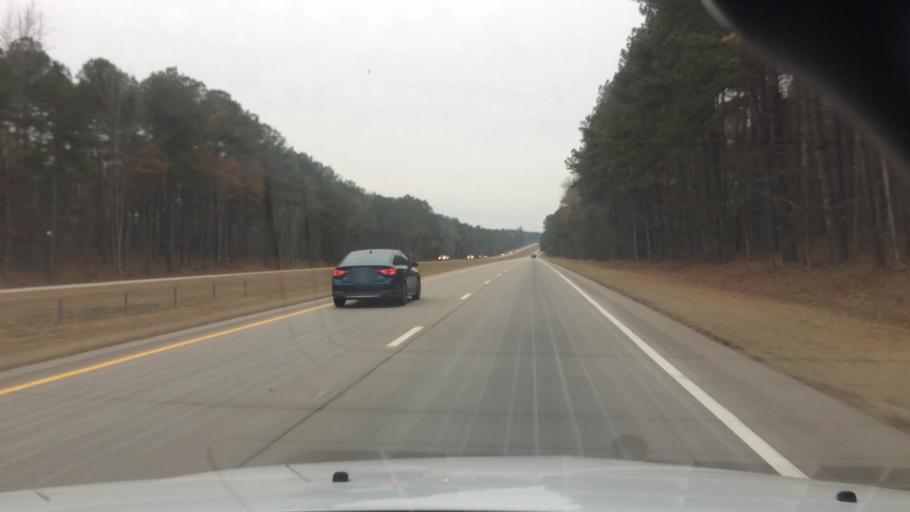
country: US
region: North Carolina
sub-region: Wake County
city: Zebulon
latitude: 35.8503
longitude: -78.2868
